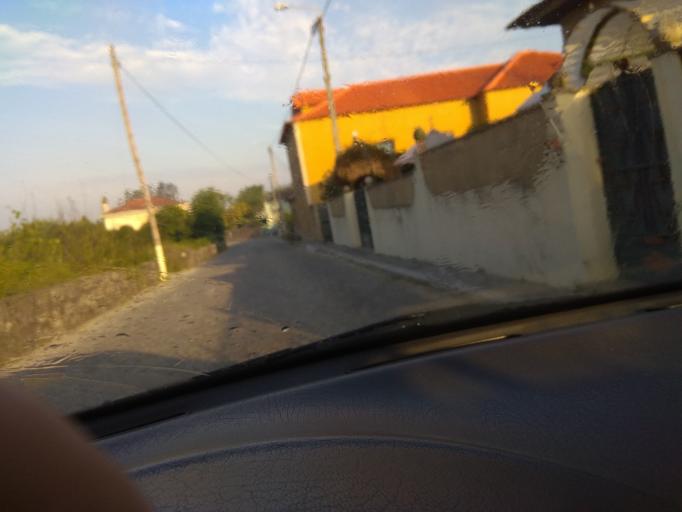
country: PT
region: Porto
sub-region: Maia
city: Nogueira
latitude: 41.2572
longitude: -8.5926
